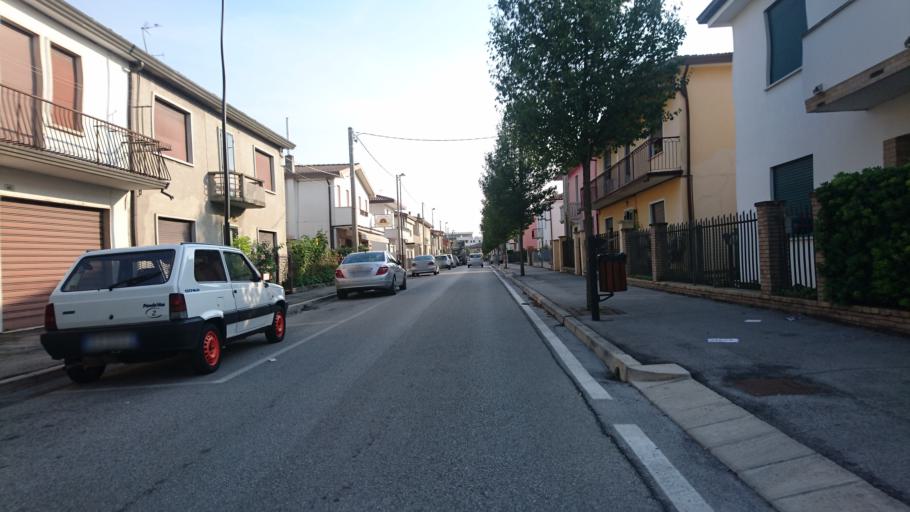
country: IT
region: Veneto
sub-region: Provincia di Padova
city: Albignasego
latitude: 45.3486
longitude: 11.8643
